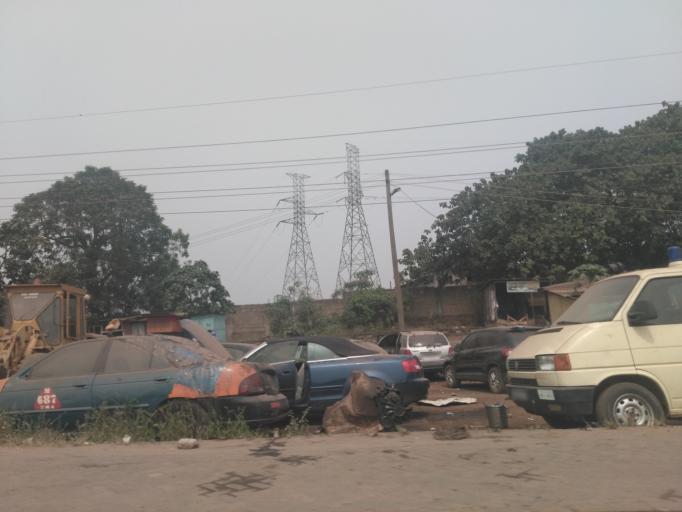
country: GH
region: Ashanti
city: Kumasi
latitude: 6.6684
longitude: -1.6110
